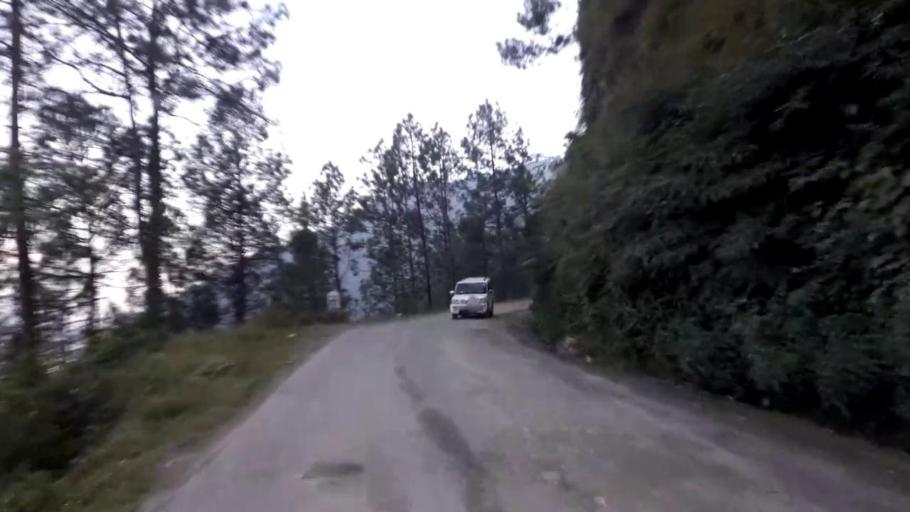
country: IN
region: Himachal Pradesh
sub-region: Shimla
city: Shimla
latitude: 31.0649
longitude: 77.1491
